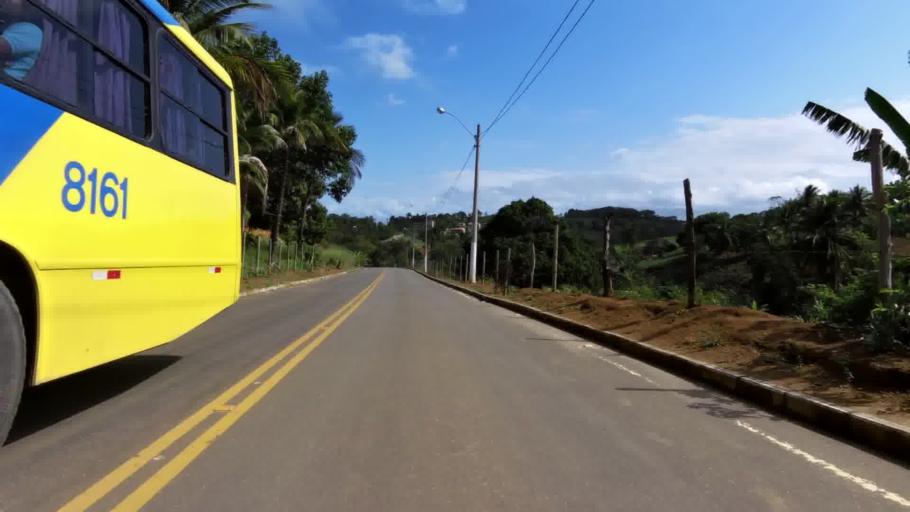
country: BR
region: Espirito Santo
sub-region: Piuma
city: Piuma
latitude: -20.8198
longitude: -40.6832
